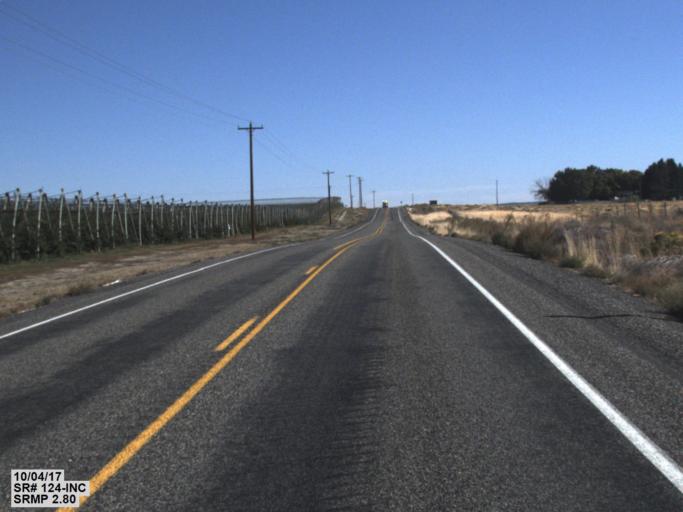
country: US
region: Washington
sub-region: Walla Walla County
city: Burbank
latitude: 46.2118
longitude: -118.9562
